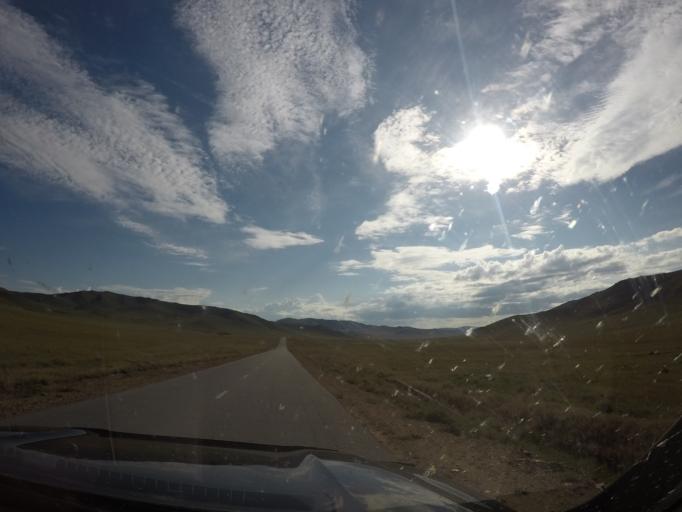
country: MN
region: Central Aimak
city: Bayandelger
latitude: 47.7078
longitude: 108.5661
